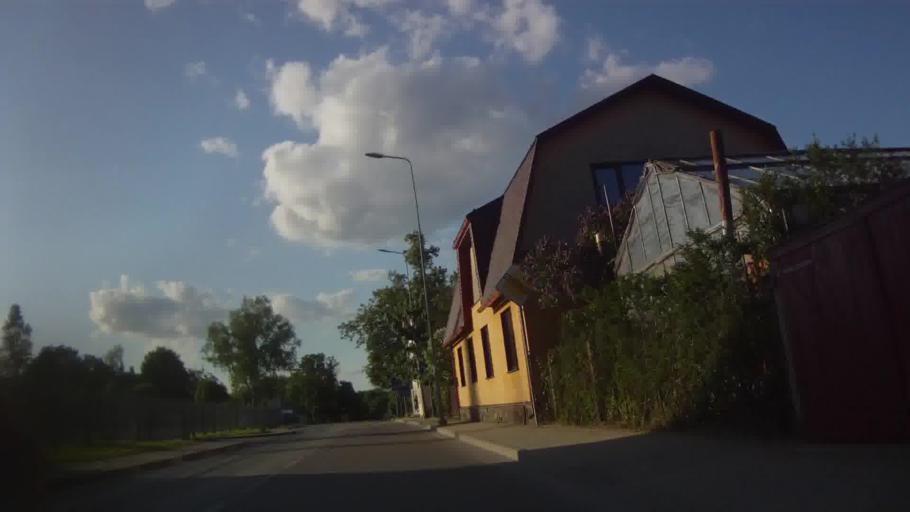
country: LV
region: Rezekne
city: Rezekne
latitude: 56.4994
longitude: 27.3413
